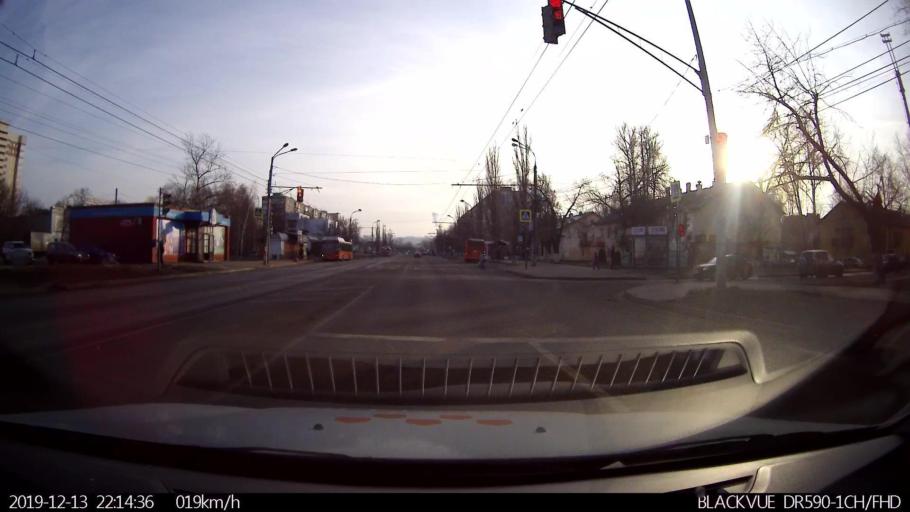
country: RU
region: Nizjnij Novgorod
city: Nizhniy Novgorod
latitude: 56.2649
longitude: 43.8941
